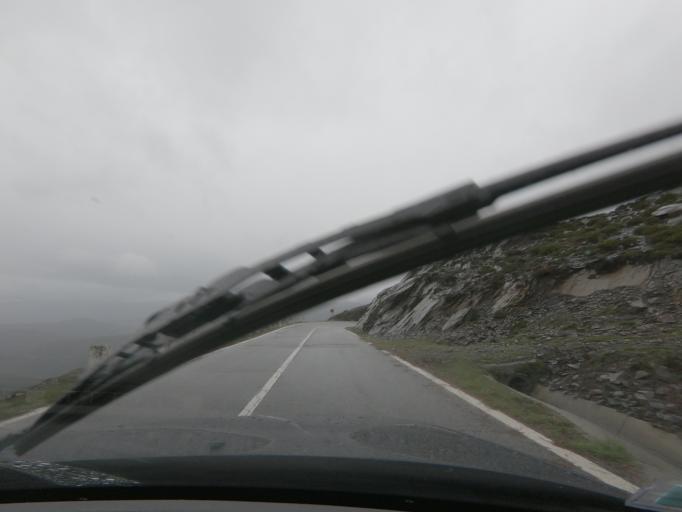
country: PT
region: Vila Real
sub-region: Mondim de Basto
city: Mondim de Basto
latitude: 41.3380
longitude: -7.8773
